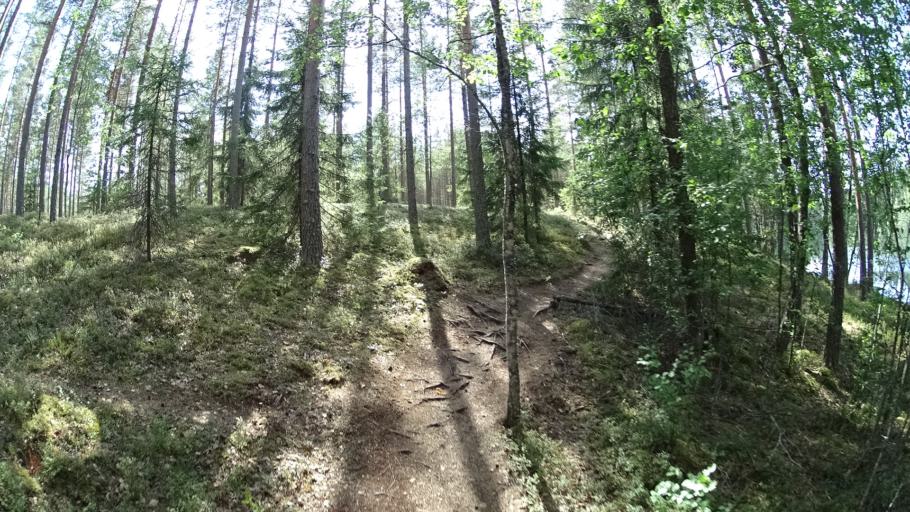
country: FI
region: Uusimaa
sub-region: Helsinki
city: Kaerkoelae
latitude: 60.7340
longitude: 24.0664
